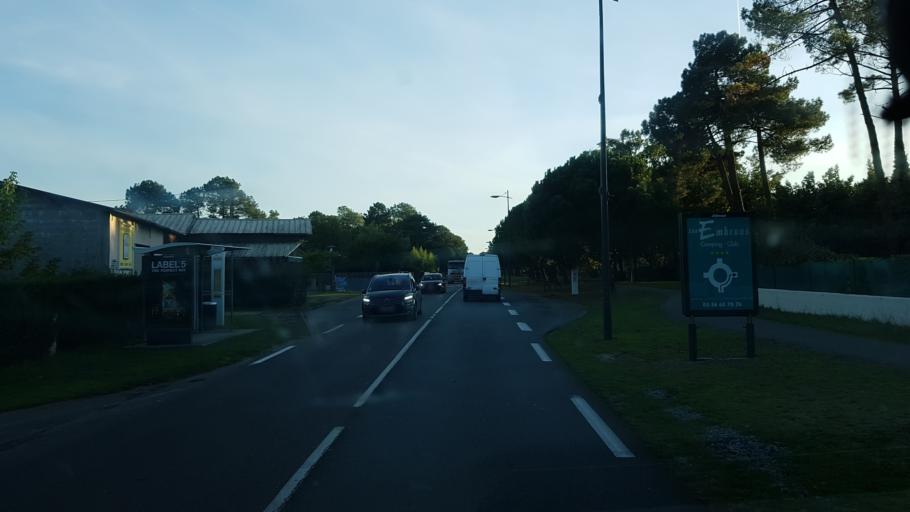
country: FR
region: Aquitaine
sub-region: Departement de la Gironde
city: Ares
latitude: 44.7566
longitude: -1.1801
